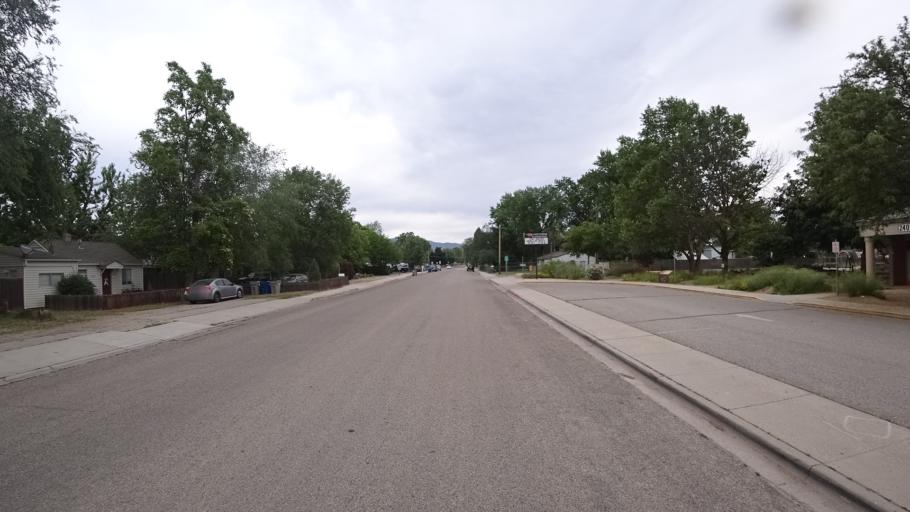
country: US
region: Idaho
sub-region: Ada County
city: Boise
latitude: 43.5825
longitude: -116.2108
